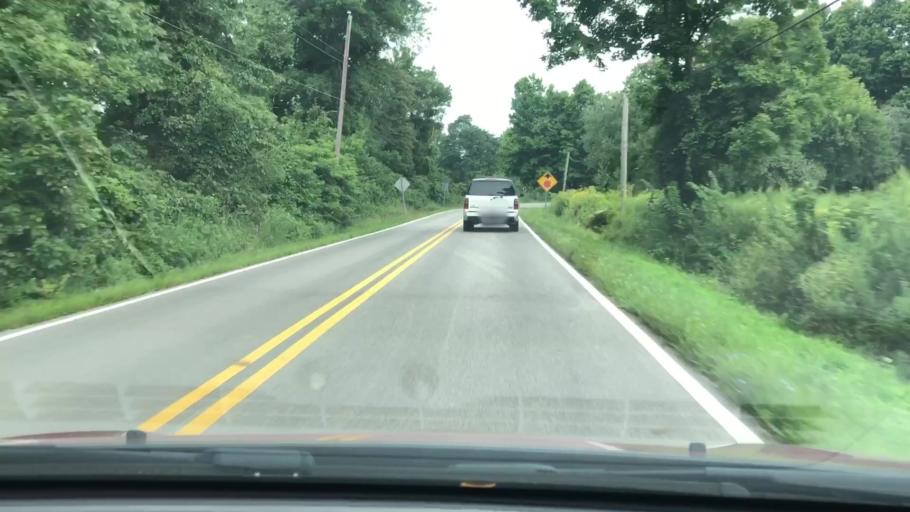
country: US
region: Ohio
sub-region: Delaware County
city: Sunbury
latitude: 40.1868
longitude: -82.8532
